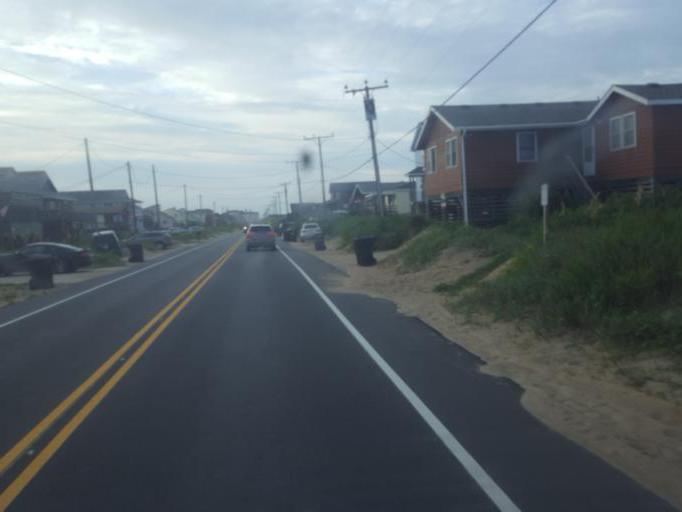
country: US
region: North Carolina
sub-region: Dare County
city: Kitty Hawk
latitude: 36.0921
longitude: -75.7063
